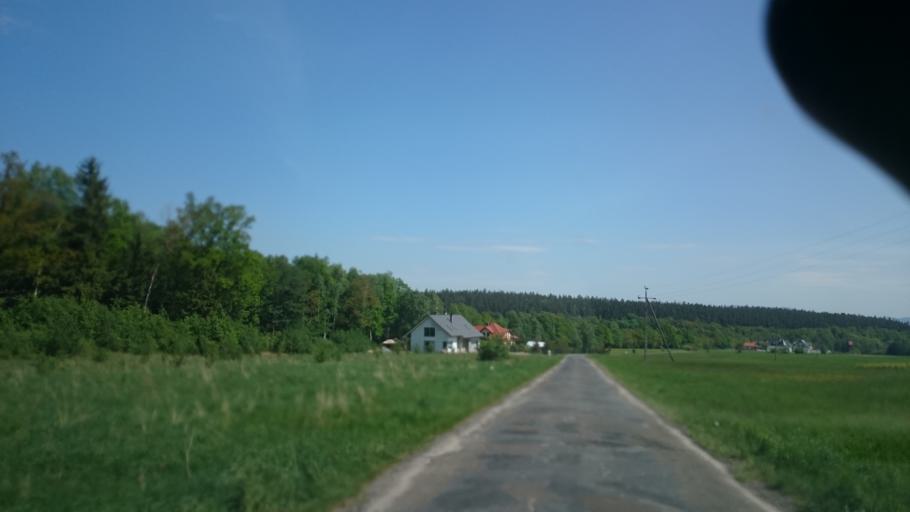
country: PL
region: Lower Silesian Voivodeship
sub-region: Powiat klodzki
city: Polanica-Zdroj
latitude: 50.3660
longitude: 16.5336
